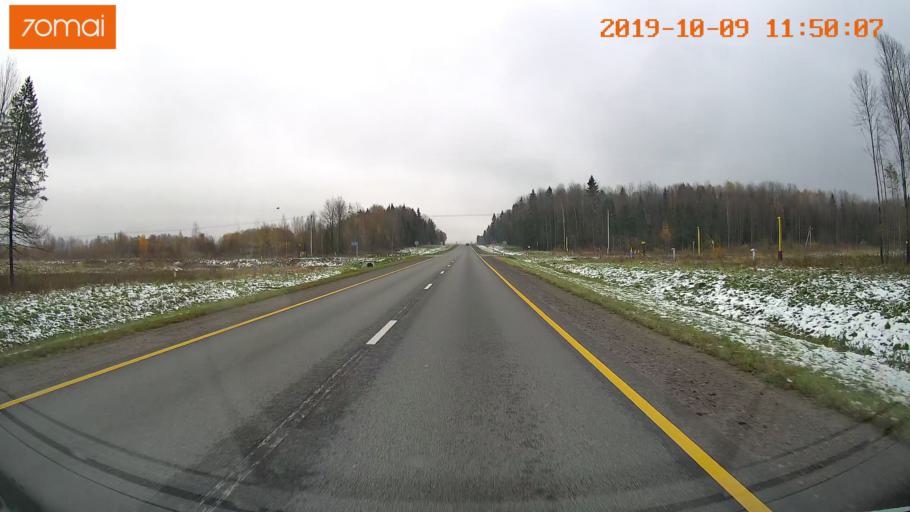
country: RU
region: Vologda
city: Gryazovets
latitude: 58.8098
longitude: 40.2410
